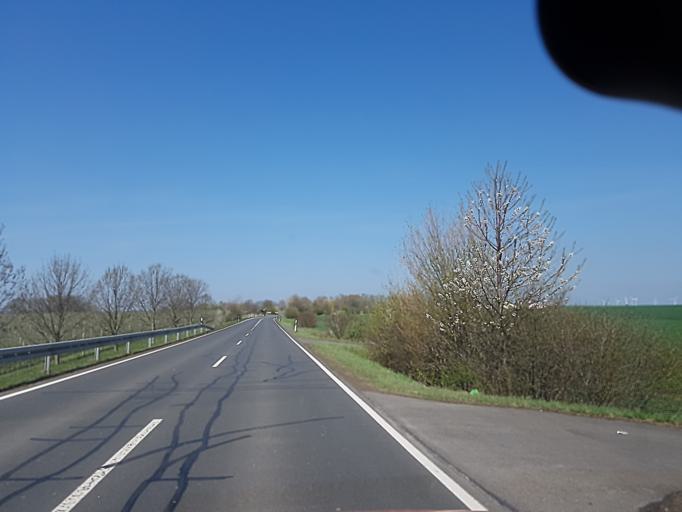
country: DE
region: Saxony
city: Ostrau
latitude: 51.1968
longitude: 12.8922
